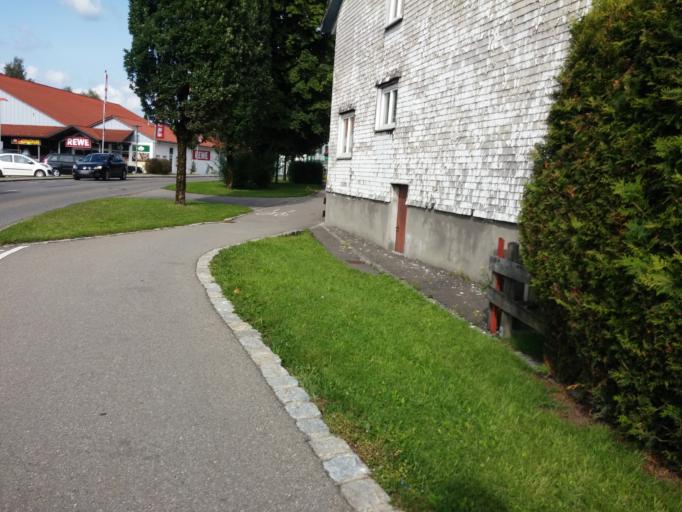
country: DE
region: Baden-Wuerttemberg
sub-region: Tuebingen Region
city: Isny im Allgau
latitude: 47.6958
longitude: 10.0408
